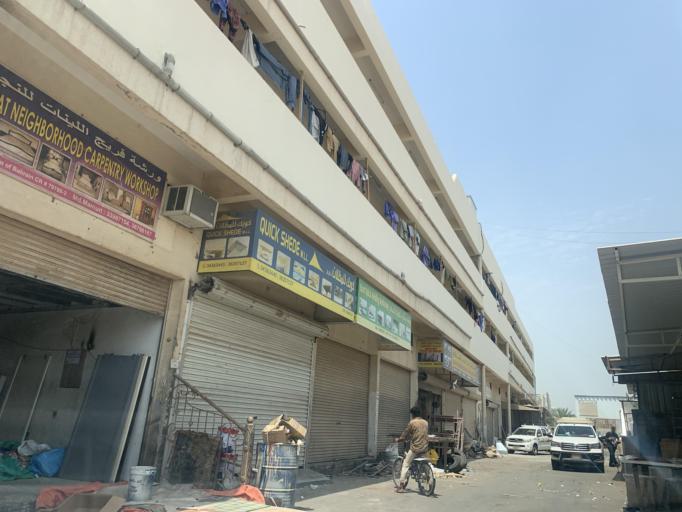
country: BH
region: Central Governorate
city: Madinat Hamad
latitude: 26.1422
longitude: 50.4887
